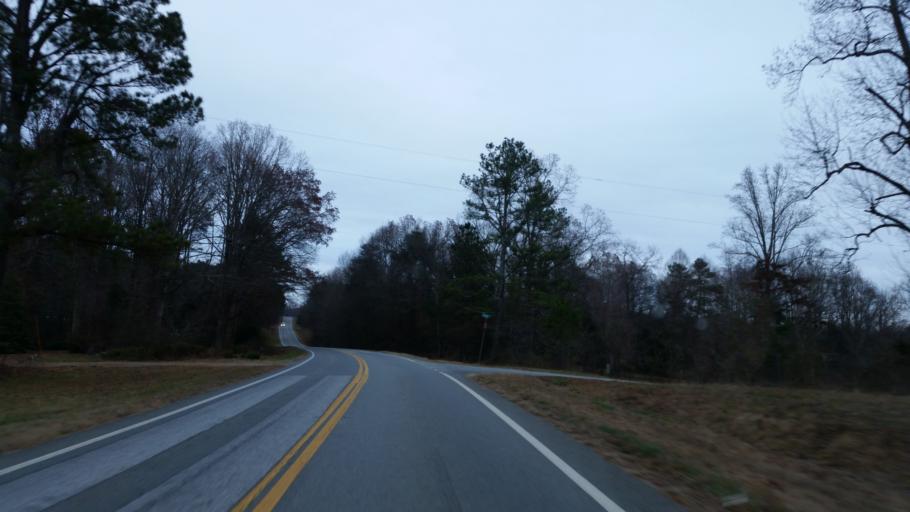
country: US
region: Georgia
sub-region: Dawson County
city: Dawsonville
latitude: 34.4915
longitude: -84.1833
